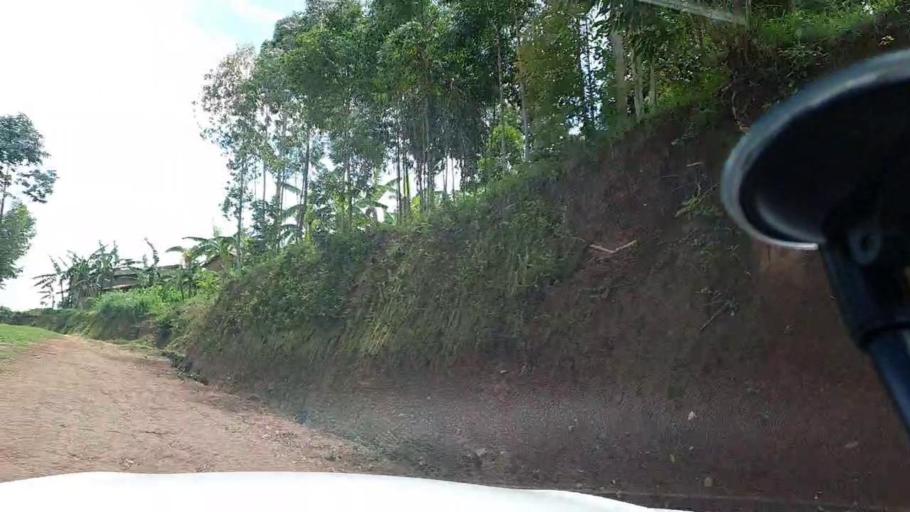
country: RW
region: Southern Province
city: Gitarama
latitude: -2.0767
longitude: 29.6688
